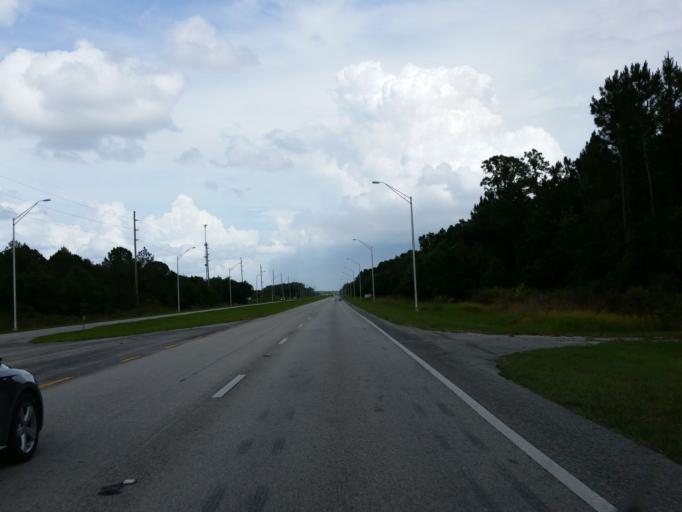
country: US
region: Florida
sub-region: Polk County
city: Babson Park
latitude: 27.8811
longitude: -81.4355
